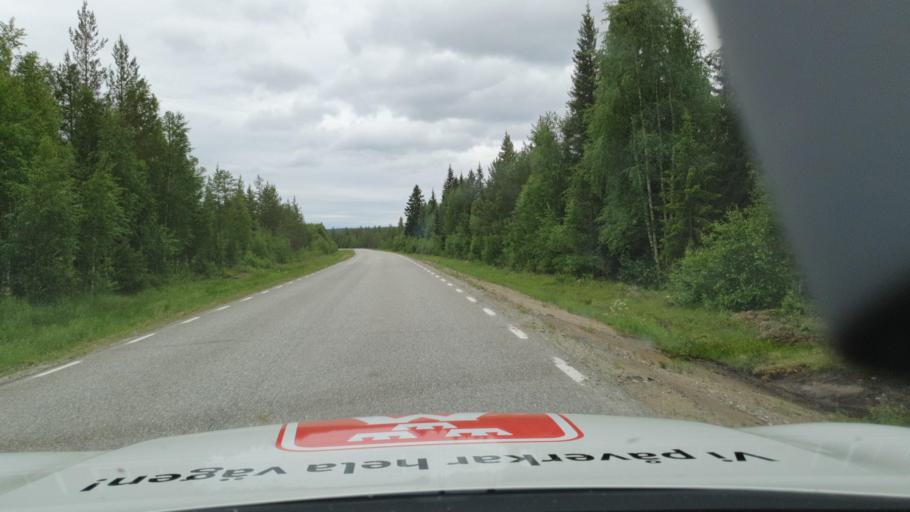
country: SE
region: Vaesterbotten
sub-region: Lycksele Kommun
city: Lycksele
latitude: 64.1870
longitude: 18.3142
